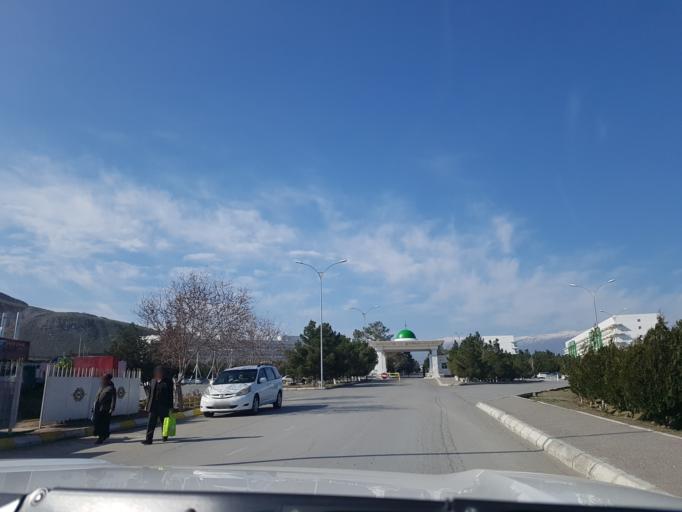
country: TM
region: Ahal
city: Baharly
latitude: 38.5175
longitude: 57.1793
